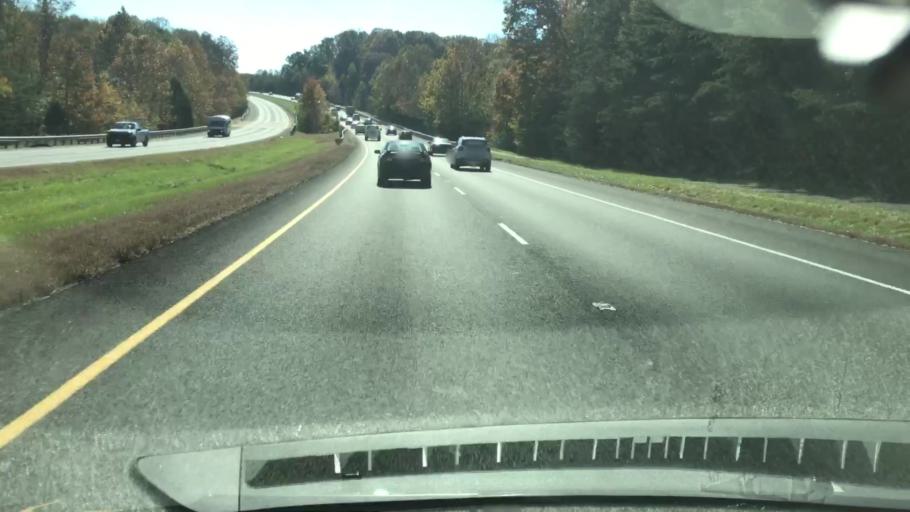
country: US
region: Virginia
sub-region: Fairfax County
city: Fairfax Station
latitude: 38.8052
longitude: -77.3434
